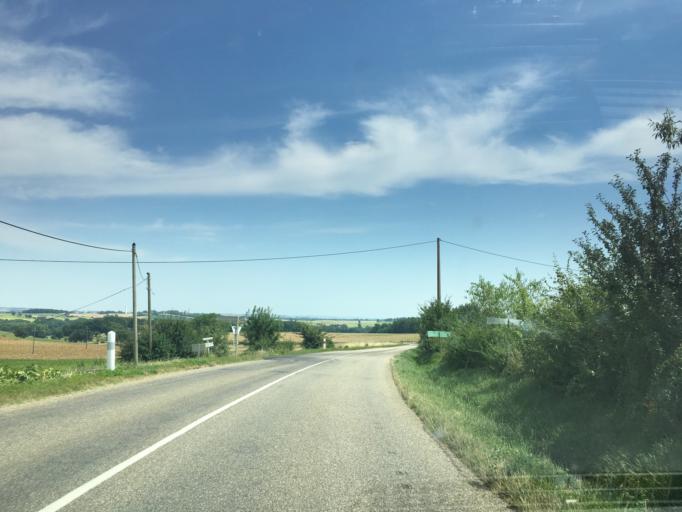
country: FR
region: Midi-Pyrenees
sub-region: Departement du Gers
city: Fleurance
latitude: 43.8632
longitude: 0.7283
